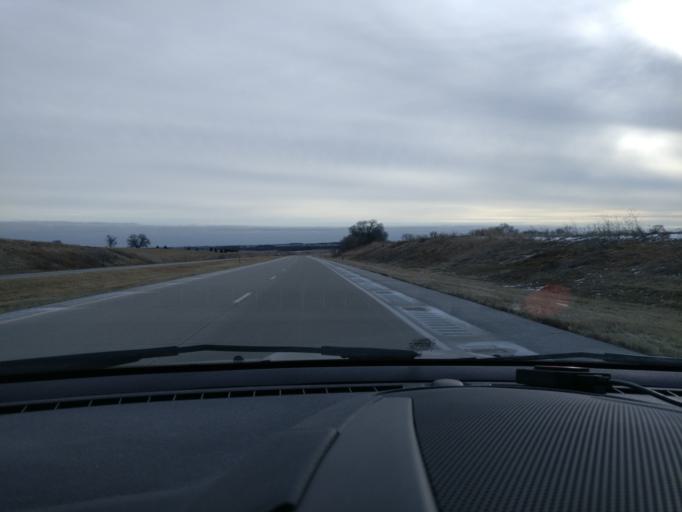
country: US
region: Nebraska
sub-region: Saunders County
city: Wahoo
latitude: 41.1290
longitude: -96.6304
